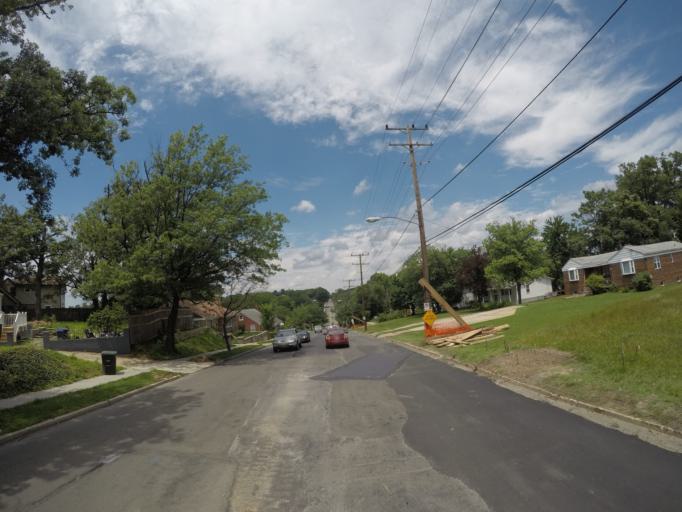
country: US
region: Maryland
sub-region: Montgomery County
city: Takoma Park
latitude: 38.9667
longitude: -77.0037
